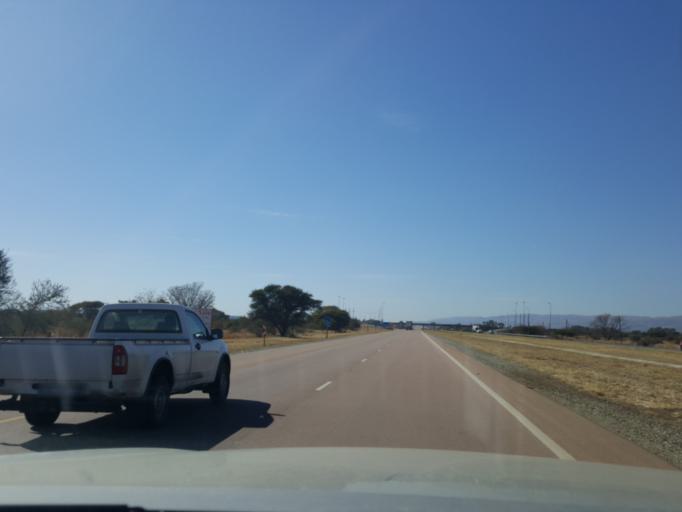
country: ZA
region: North-West
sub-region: Bojanala Platinum District Municipality
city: Brits
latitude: -25.7373
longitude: 27.5480
